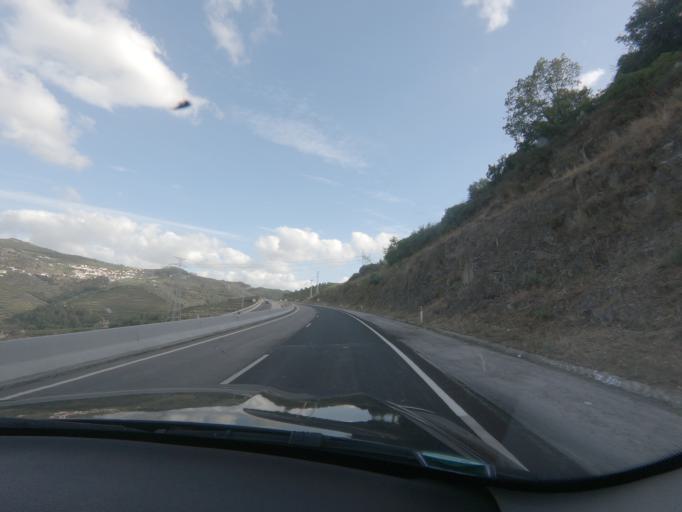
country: PT
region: Viseu
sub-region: Lamego
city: Lamego
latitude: 41.1163
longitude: -7.7794
